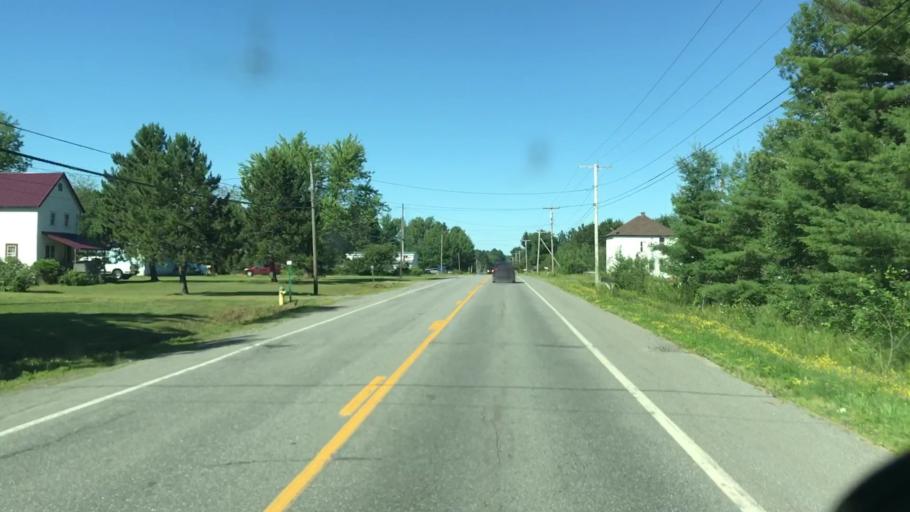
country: US
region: Maine
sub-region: Penobscot County
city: Lincoln
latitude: 45.3507
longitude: -68.5401
